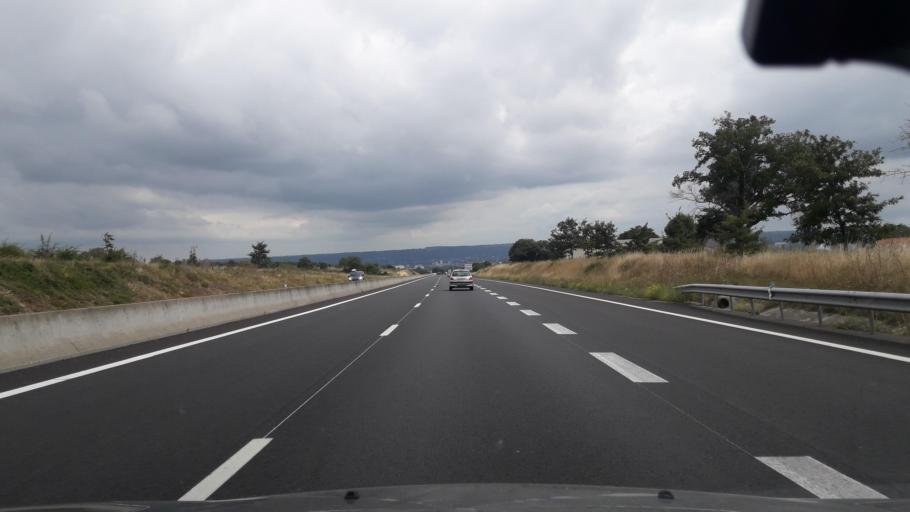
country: FR
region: Auvergne
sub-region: Departement de l'Allier
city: Premilhat
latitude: 46.3221
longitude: 2.5234
